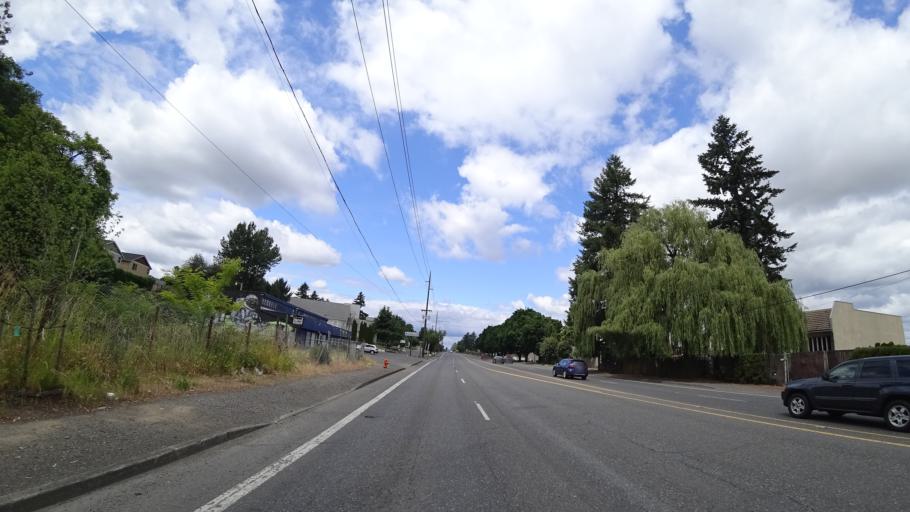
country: US
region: Oregon
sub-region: Multnomah County
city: Portland
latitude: 45.5673
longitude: -122.6022
